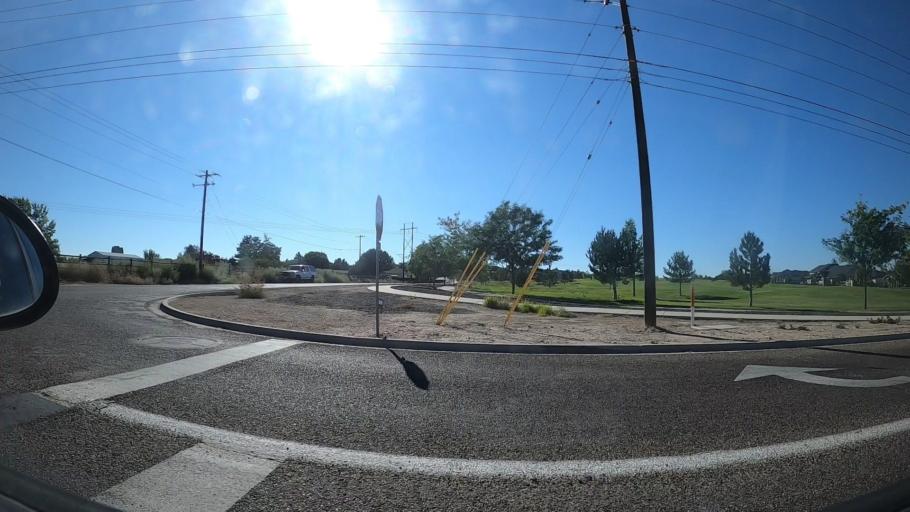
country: US
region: Idaho
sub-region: Canyon County
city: Nampa
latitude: 43.5491
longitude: -116.6126
